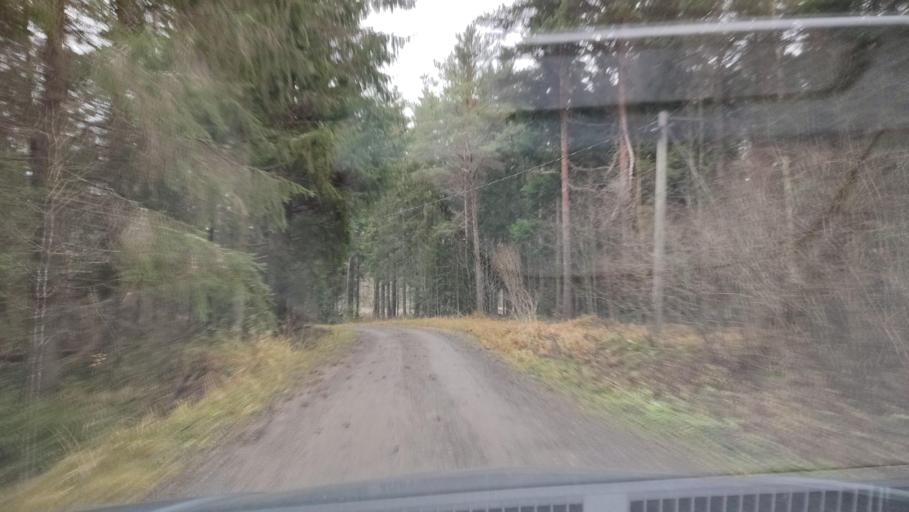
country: FI
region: Ostrobothnia
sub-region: Sydosterbotten
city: Kristinestad
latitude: 62.2778
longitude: 21.4133
